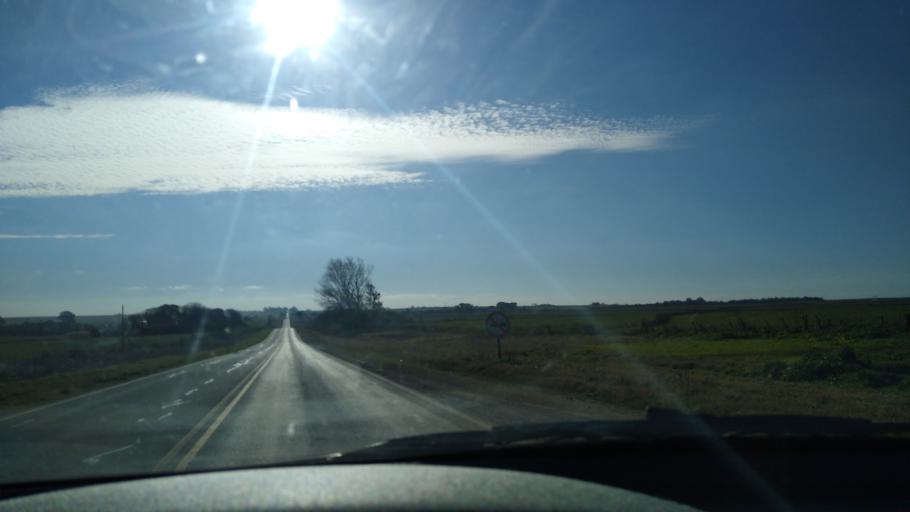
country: AR
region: Entre Rios
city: Aranguren
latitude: -32.3623
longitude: -60.3482
